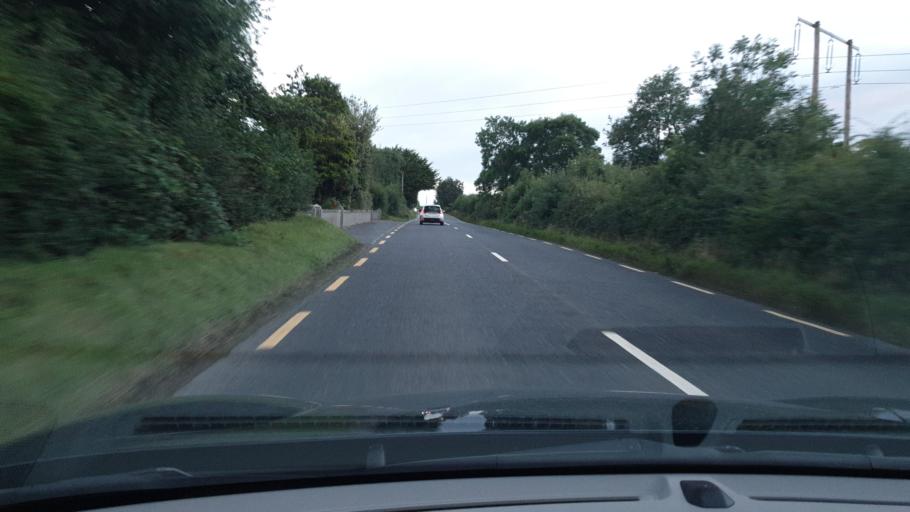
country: IE
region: Leinster
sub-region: An Mhi
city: Duleek
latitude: 53.6095
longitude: -6.4339
